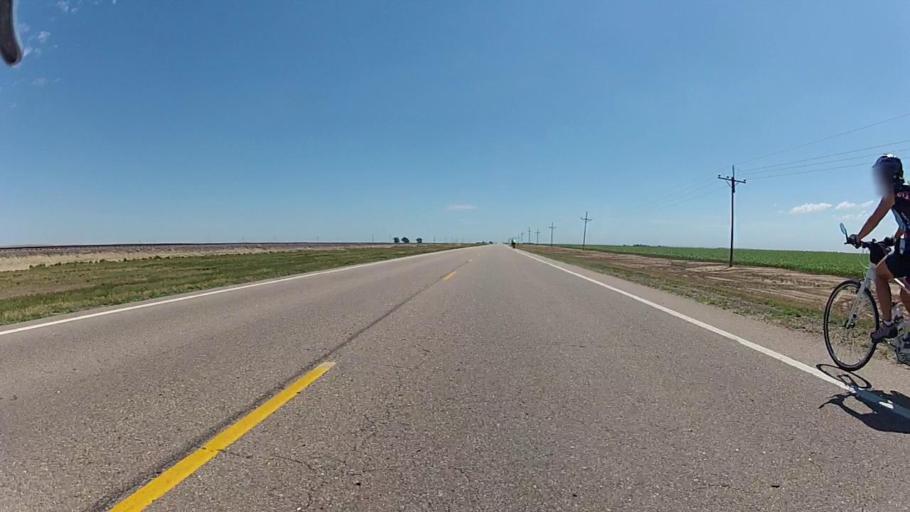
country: US
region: Kansas
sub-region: Gray County
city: Cimarron
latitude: 37.6595
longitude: -100.2187
